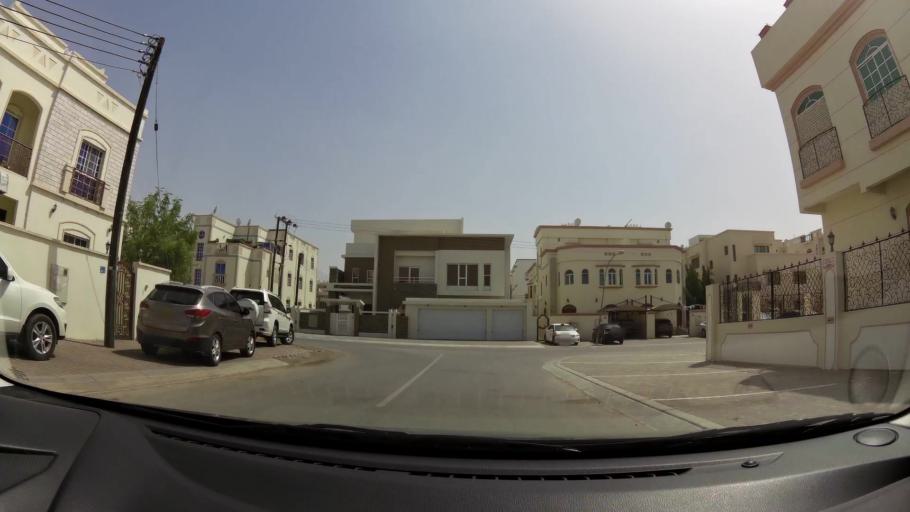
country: OM
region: Muhafazat Masqat
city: Bawshar
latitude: 23.5671
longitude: 58.3863
